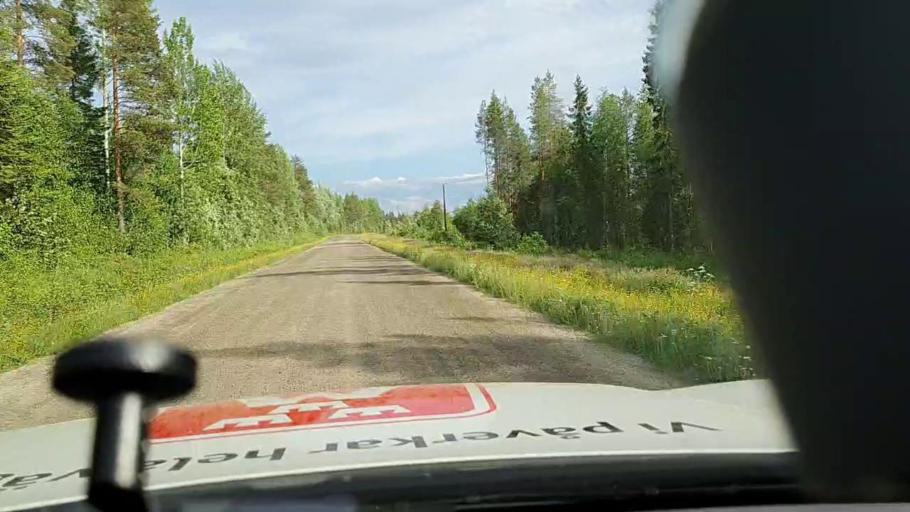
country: SE
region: Norrbotten
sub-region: Alvsbyns Kommun
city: AElvsbyn
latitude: 66.1781
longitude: 21.2351
